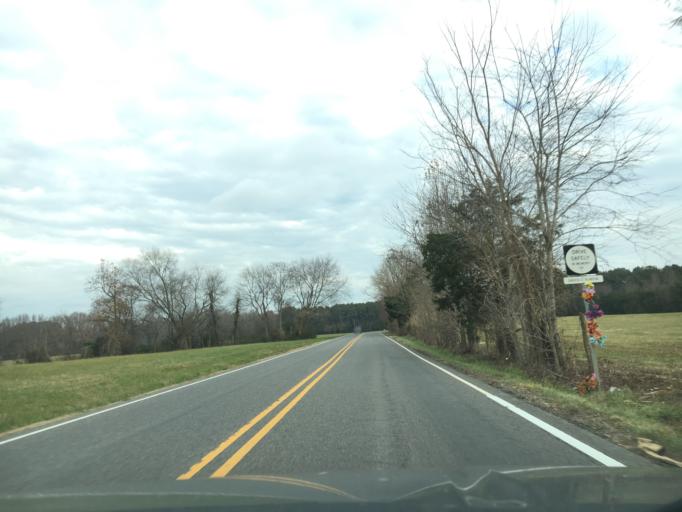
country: US
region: Virginia
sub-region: Cumberland County
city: Cumberland
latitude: 37.4595
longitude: -78.2887
